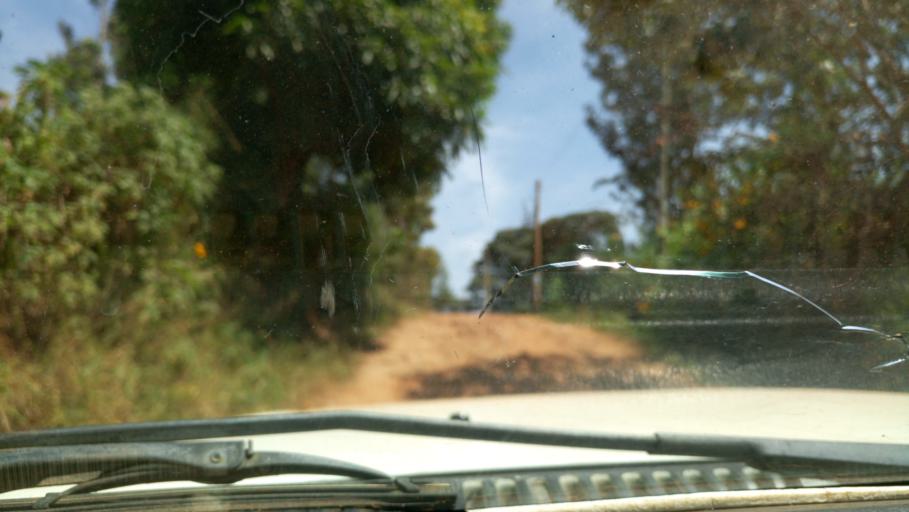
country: KE
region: Murang'a District
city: Murang'a
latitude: -0.7314
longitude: 37.1430
